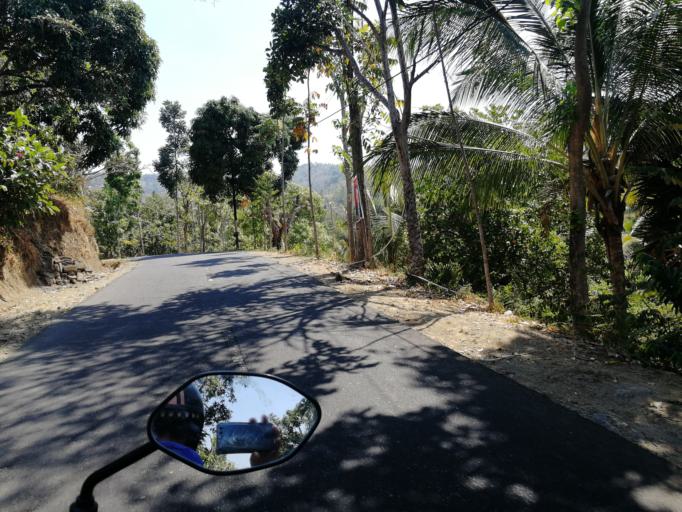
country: ID
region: Bali
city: Banjar Kedisan
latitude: -8.1379
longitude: 115.3219
